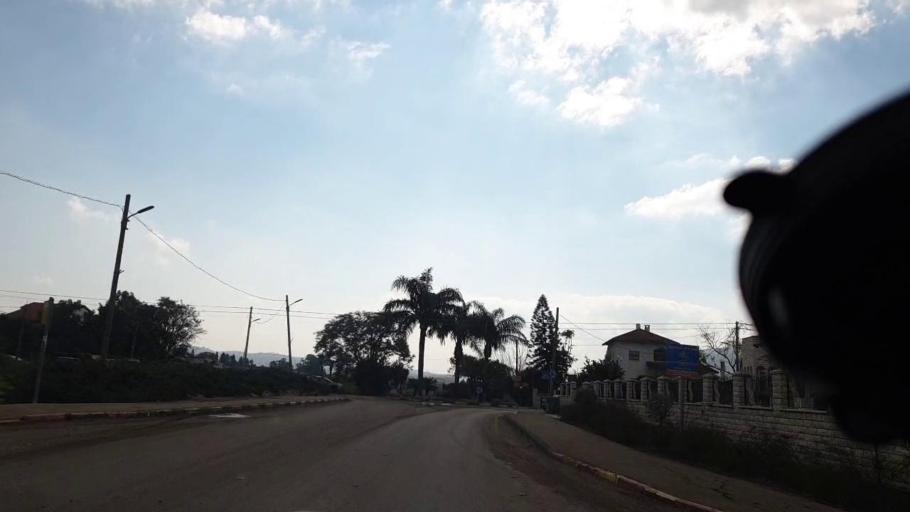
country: IL
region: Haifa
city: Rekhasim
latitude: 32.7507
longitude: 35.0877
